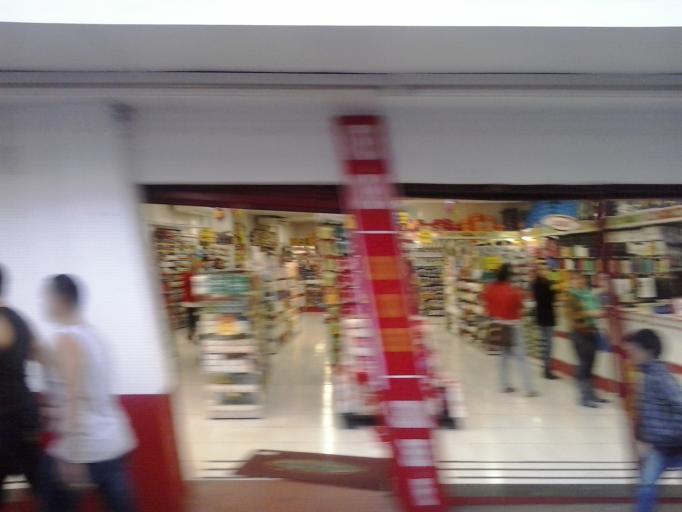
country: BR
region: Rio Grande do Sul
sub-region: Santa Maria
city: Santa Maria
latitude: -29.6872
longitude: -53.8067
